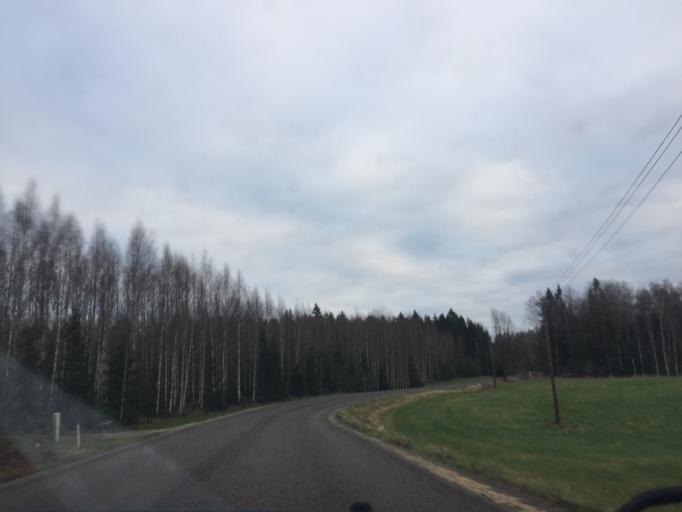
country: LV
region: Krimulda
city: Ragana
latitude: 57.1611
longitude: 24.7410
